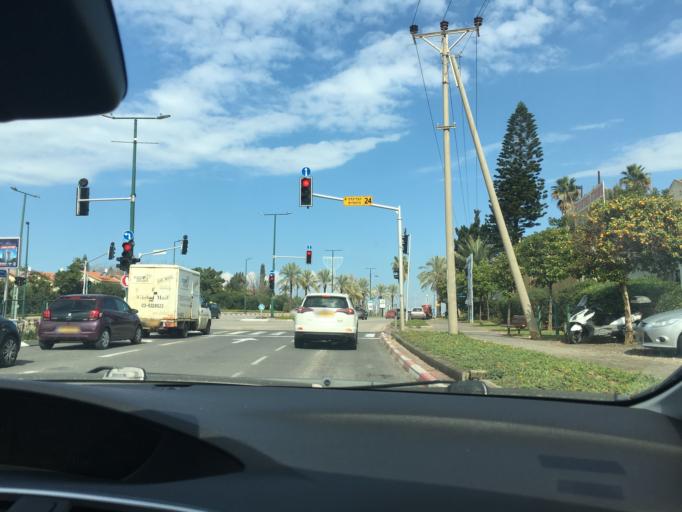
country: IL
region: Central District
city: Ra'anana
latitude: 32.1757
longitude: 34.8516
